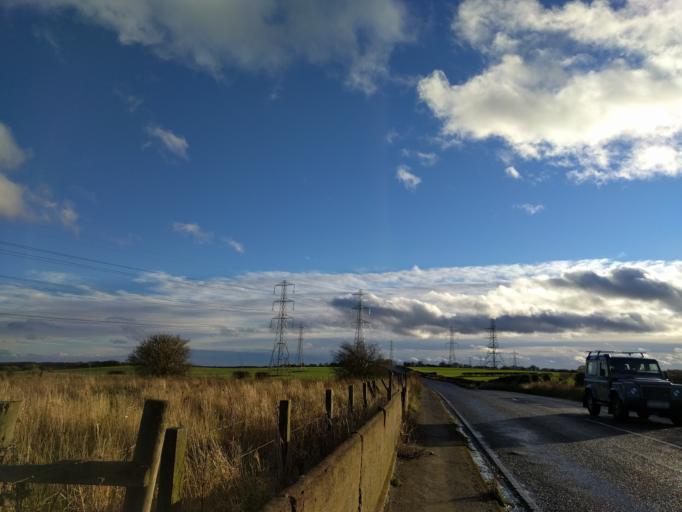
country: GB
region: England
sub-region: Northumberland
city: Bedlington
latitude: 55.1182
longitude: -1.5749
